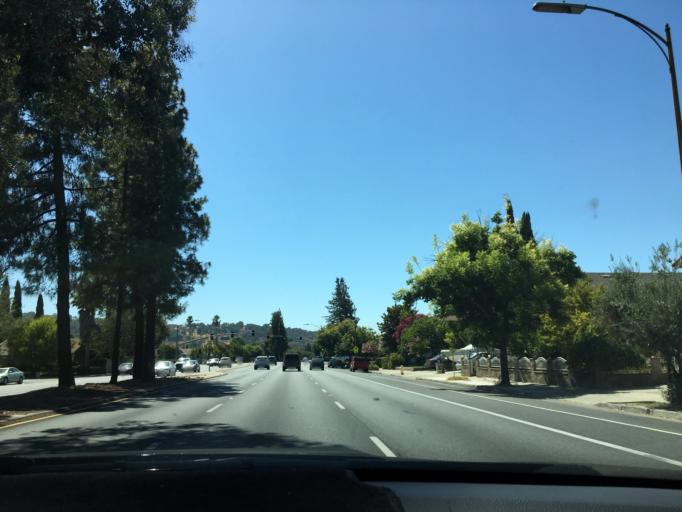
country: US
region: California
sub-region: Santa Clara County
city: Seven Trees
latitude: 37.2369
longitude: -121.8377
